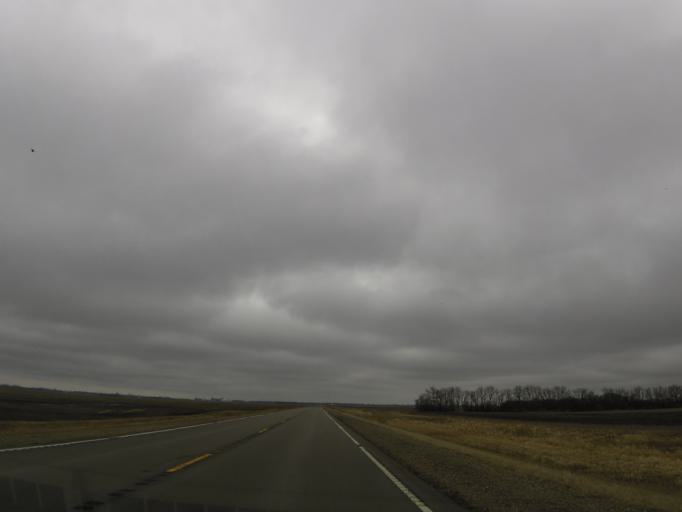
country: US
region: North Dakota
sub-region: Cass County
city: Horace
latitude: 46.6298
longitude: -97.0811
